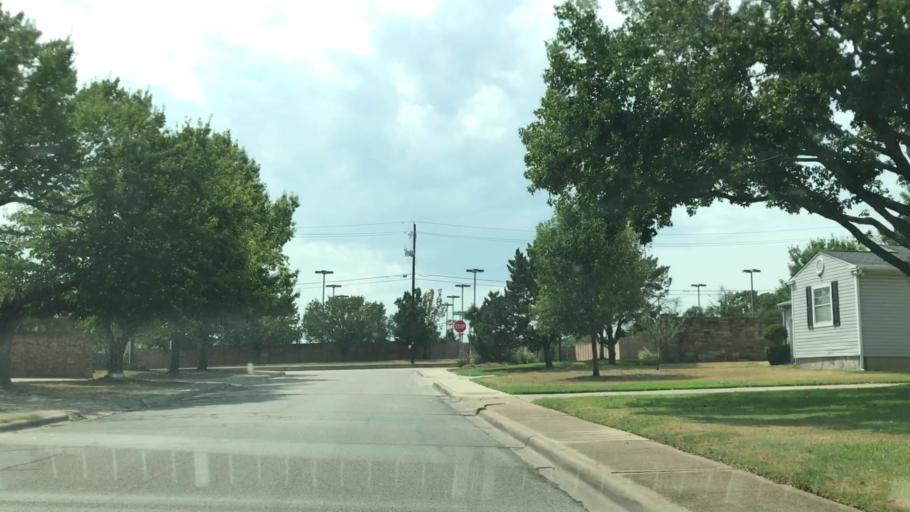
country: US
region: Texas
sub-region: Dallas County
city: Irving
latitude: 32.8402
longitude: -96.9506
